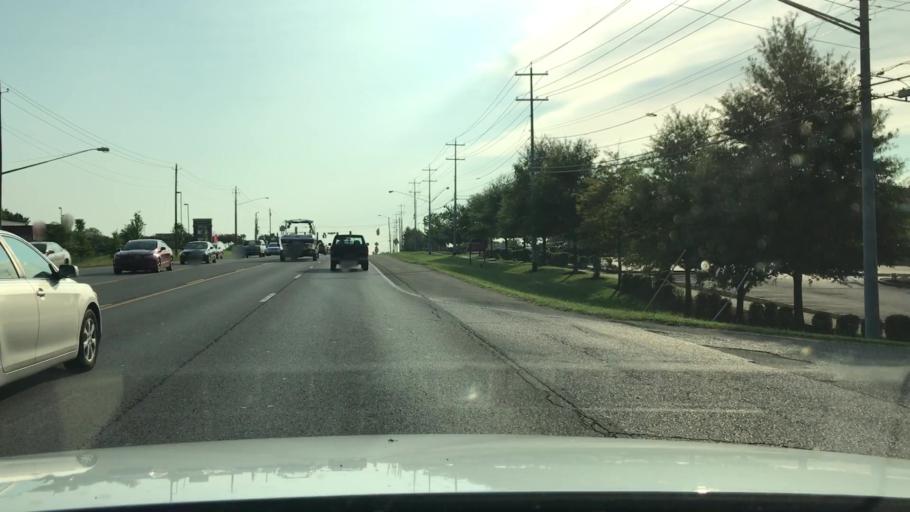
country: US
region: Tennessee
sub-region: Sumner County
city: Gallatin
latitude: 36.3753
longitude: -86.4744
